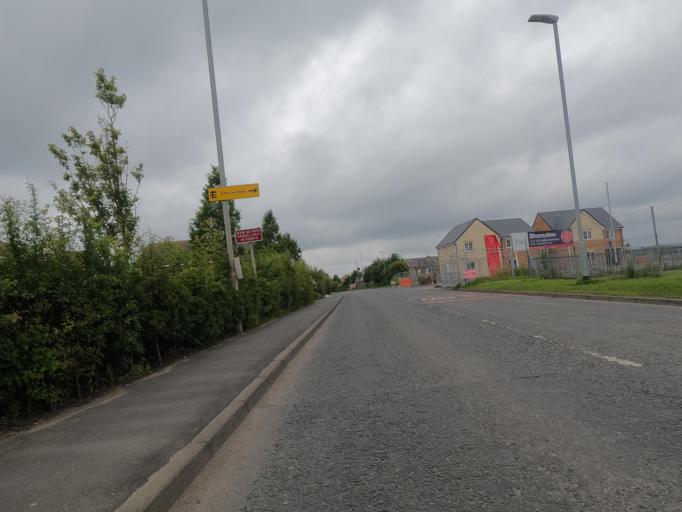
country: GB
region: England
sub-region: Northumberland
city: Blyth
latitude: 55.1063
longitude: -1.5287
